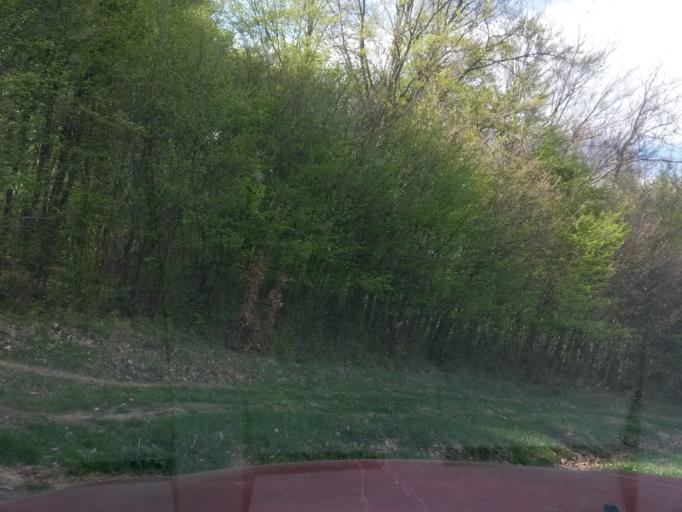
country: SK
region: Presovsky
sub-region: Okres Presov
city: Presov
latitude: 48.9468
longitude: 21.1232
